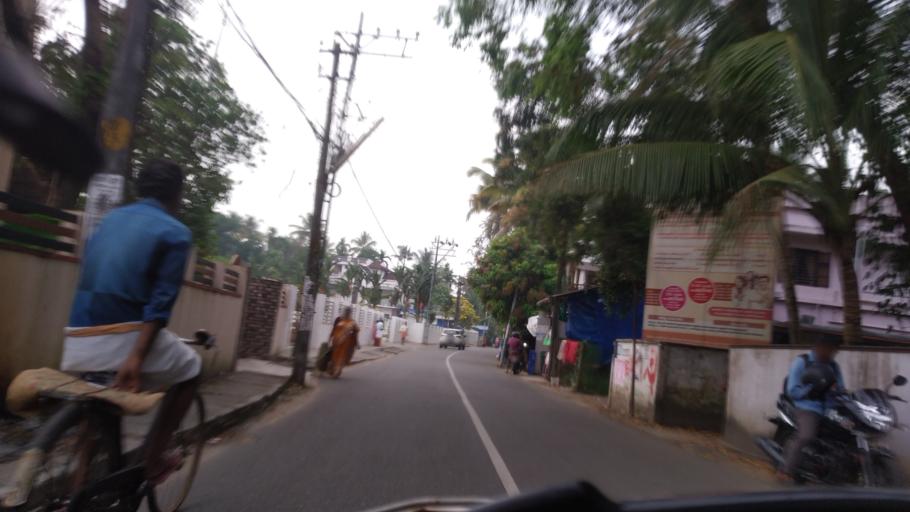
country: IN
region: Kerala
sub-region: Thrissur District
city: Kodungallur
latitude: 10.1371
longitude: 76.2201
